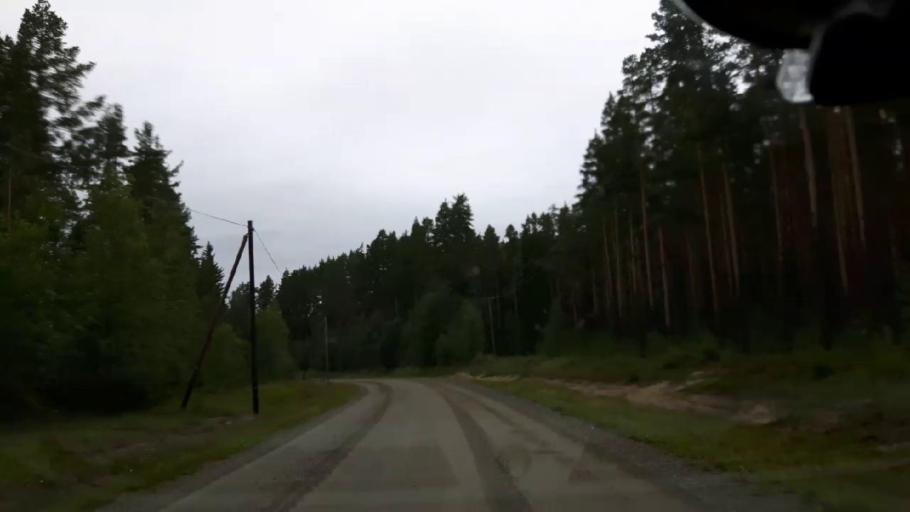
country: SE
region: Vaesternorrland
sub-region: Ange Kommun
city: Fransta
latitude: 62.7866
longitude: 16.0629
